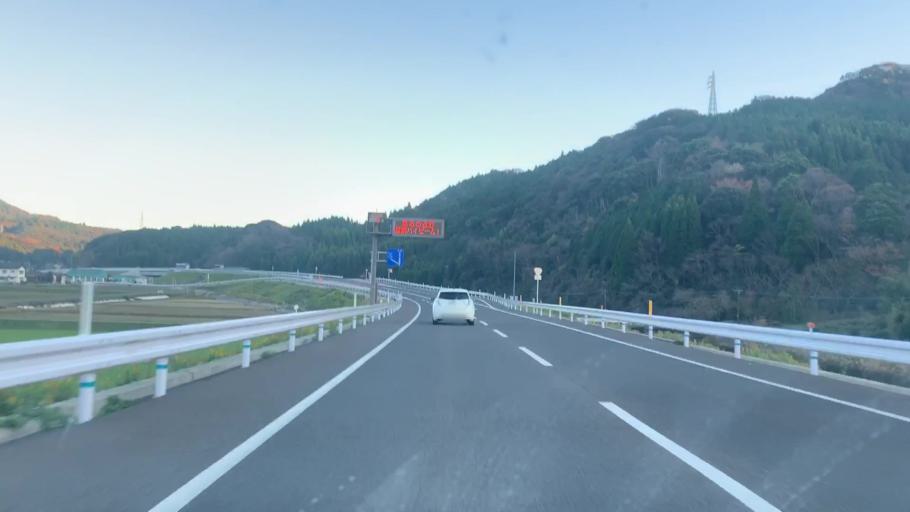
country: JP
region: Saga Prefecture
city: Takeocho-takeo
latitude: 33.2518
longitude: 129.9908
